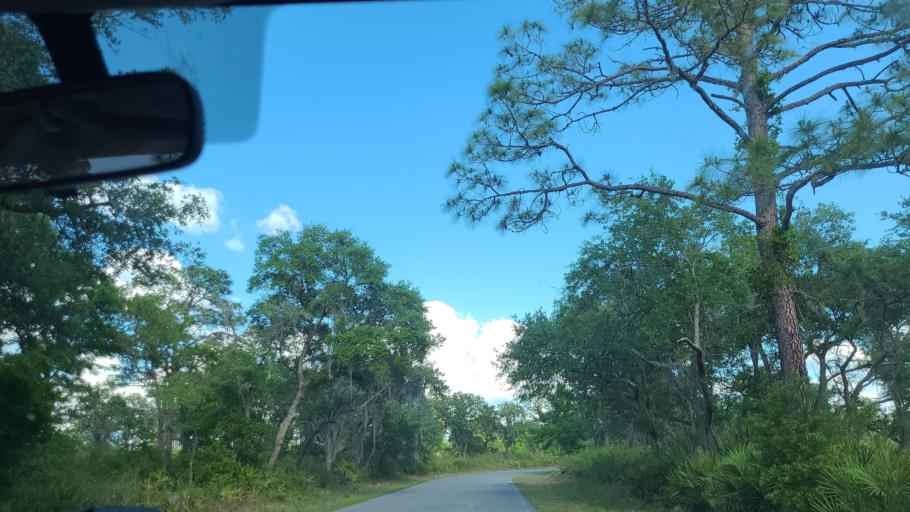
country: US
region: Florida
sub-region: Polk County
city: Babson Park
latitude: 27.9591
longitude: -81.3791
